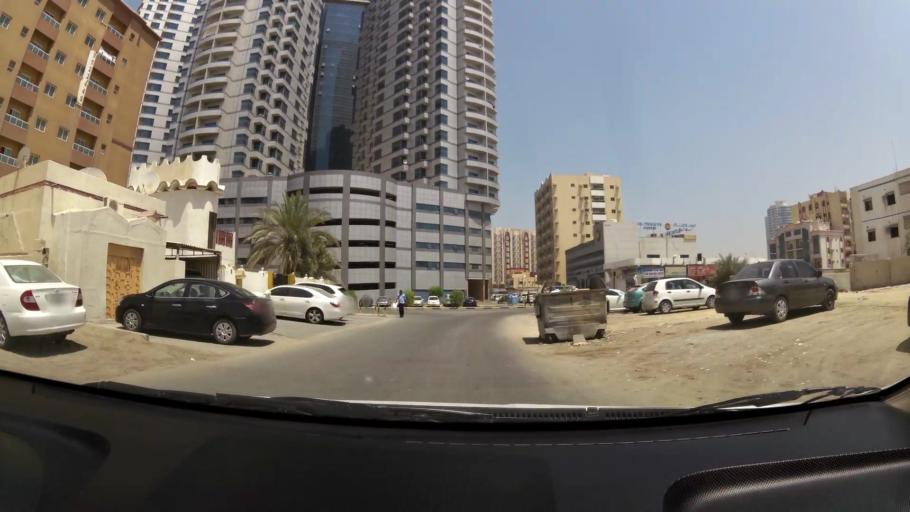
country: AE
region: Ajman
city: Ajman
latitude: 25.3986
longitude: 55.4500
